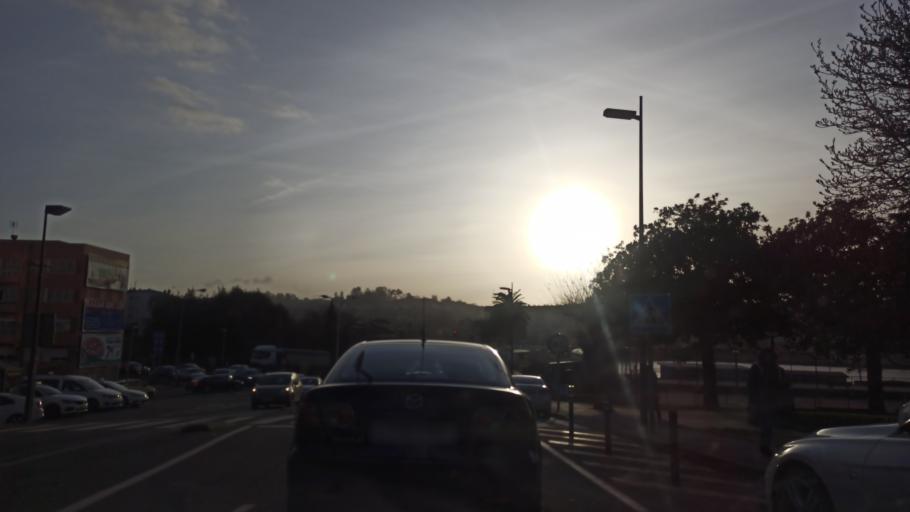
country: ES
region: Galicia
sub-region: Provincia da Coruna
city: Cambre
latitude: 43.3166
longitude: -8.3580
